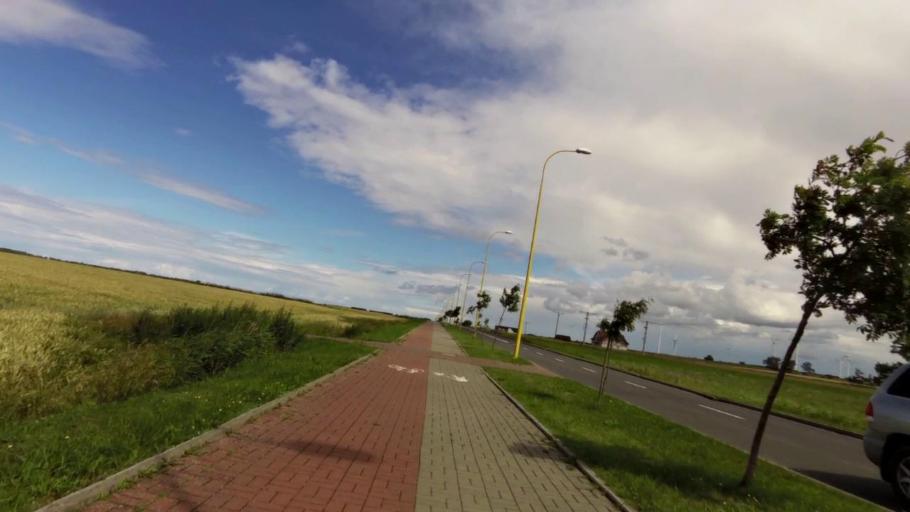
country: PL
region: West Pomeranian Voivodeship
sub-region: Powiat slawienski
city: Darlowo
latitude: 54.4327
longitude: 16.4120
